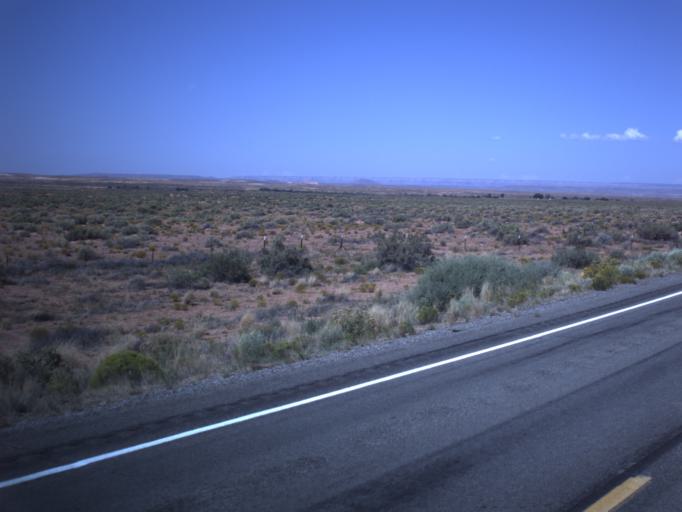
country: US
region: Utah
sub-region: San Juan County
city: Blanding
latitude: 37.1252
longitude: -109.5466
